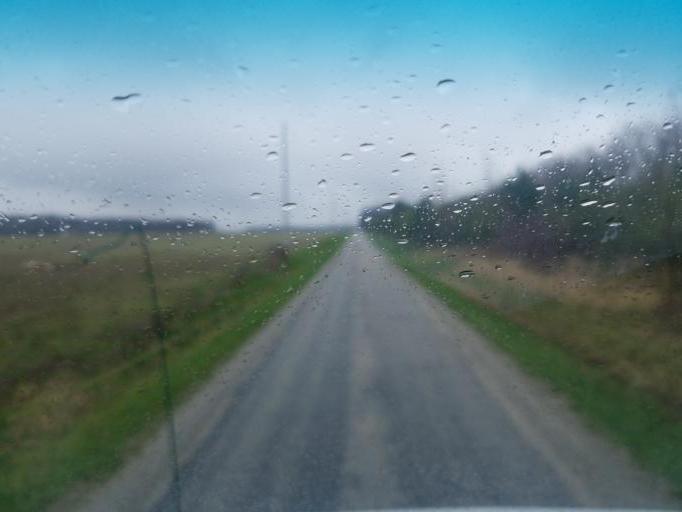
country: US
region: Ohio
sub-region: Crawford County
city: Bucyrus
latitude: 40.9216
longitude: -82.9973
